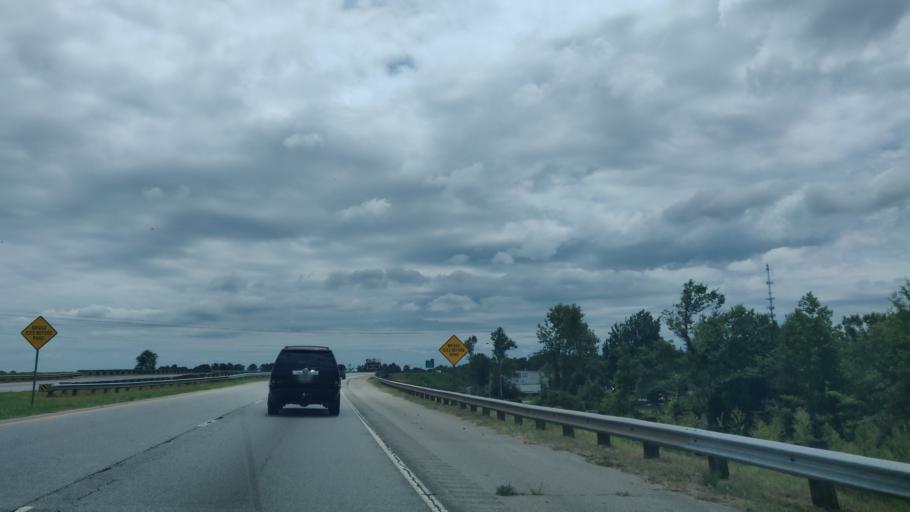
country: US
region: Georgia
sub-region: Dougherty County
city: Albany
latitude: 31.5892
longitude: -84.1171
